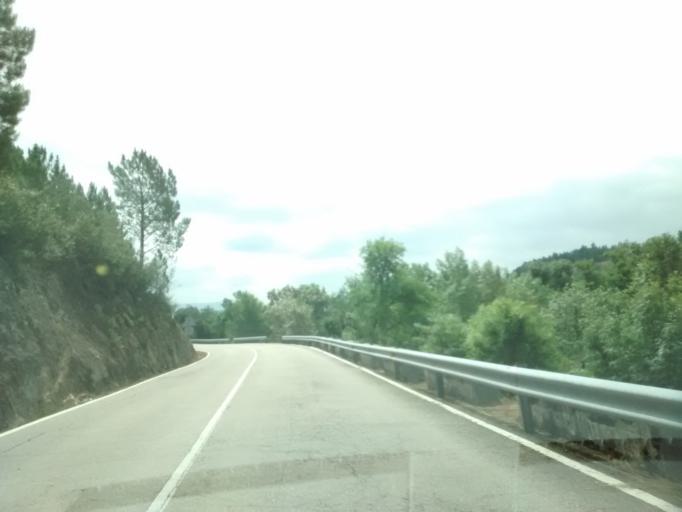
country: ES
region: Galicia
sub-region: Provincia de Ourense
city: Petin
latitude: 42.3448
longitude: -7.1792
